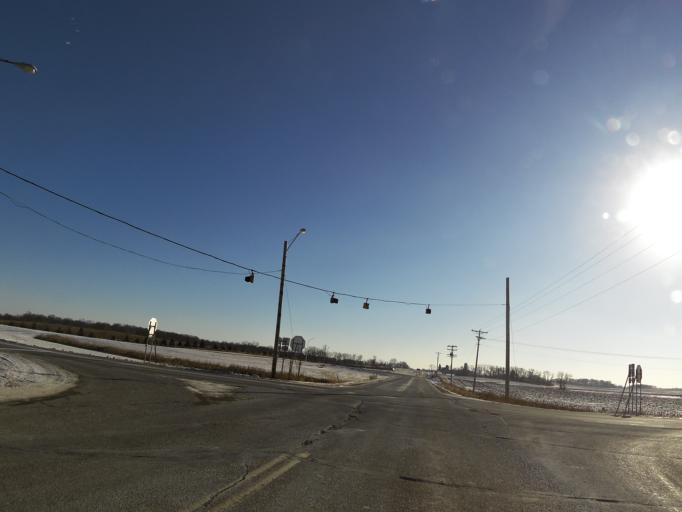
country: US
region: Minnesota
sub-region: Scott County
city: Prior Lake
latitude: 44.6892
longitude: -93.5010
